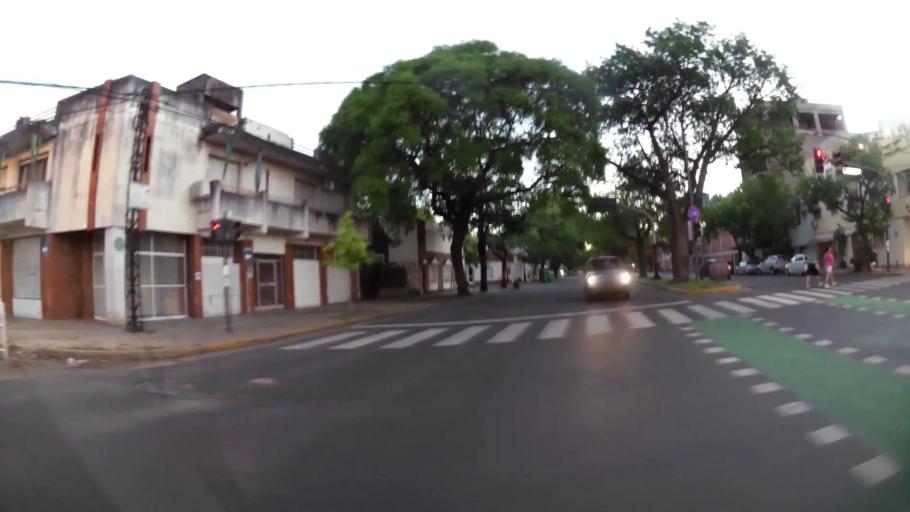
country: AR
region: Santa Fe
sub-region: Departamento de Rosario
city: Rosario
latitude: -32.9560
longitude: -60.6691
